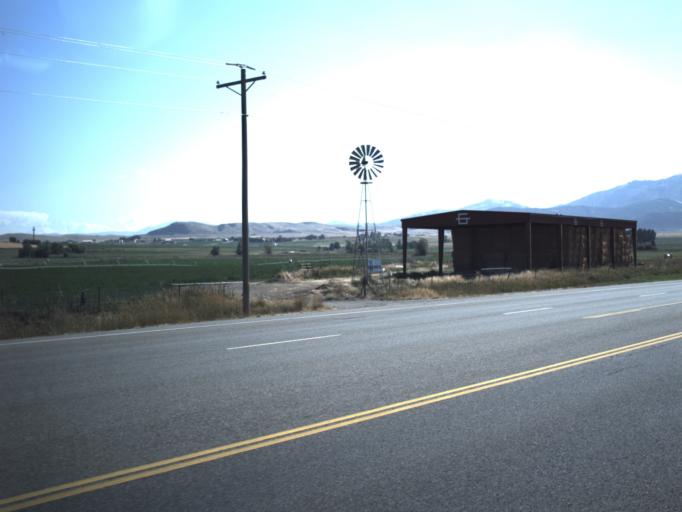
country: US
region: Utah
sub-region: Cache County
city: Wellsville
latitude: 41.6312
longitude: -111.9230
